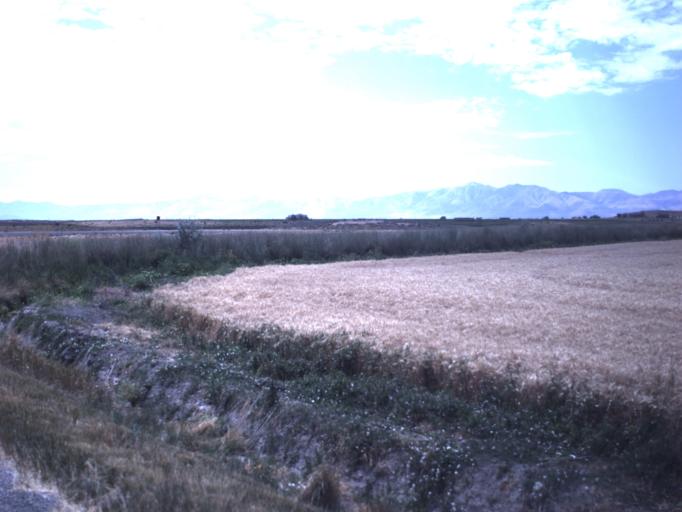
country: US
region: Utah
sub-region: Box Elder County
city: Tremonton
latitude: 41.6384
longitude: -112.3140
